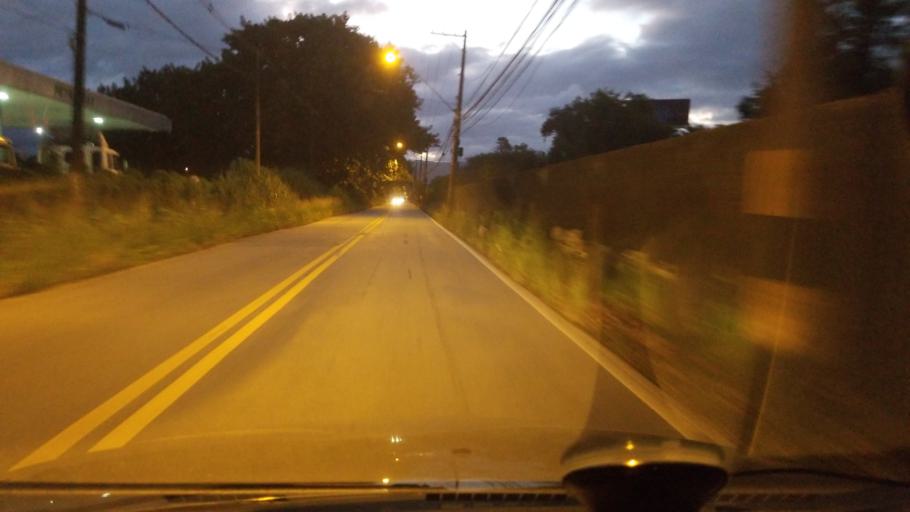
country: BR
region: Sao Paulo
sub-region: Sao Vicente
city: Sao Vicente
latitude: -23.9256
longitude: -46.3837
